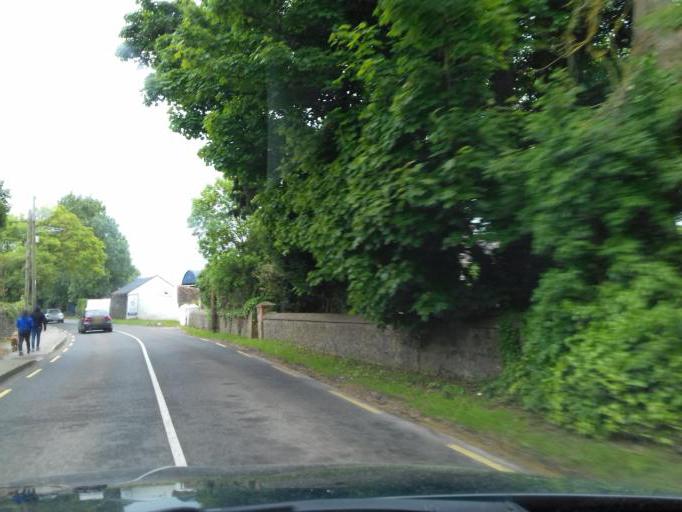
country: IE
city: Darndale
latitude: 53.4230
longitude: -6.1863
